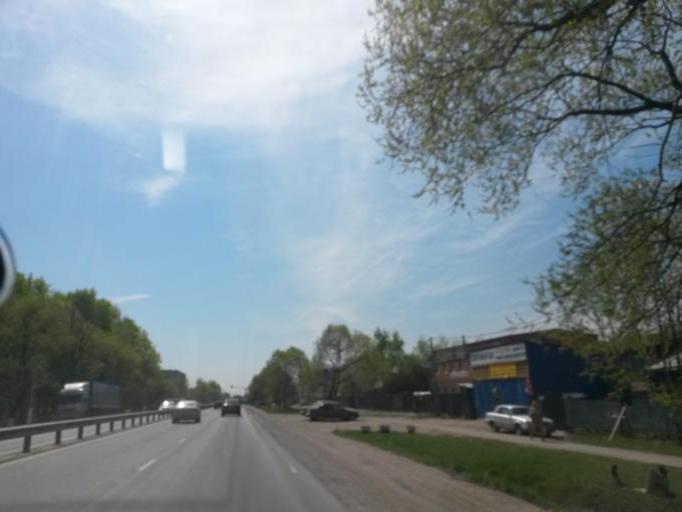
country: RU
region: Moskovskaya
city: Shcherbinka
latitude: 55.4763
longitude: 37.5638
